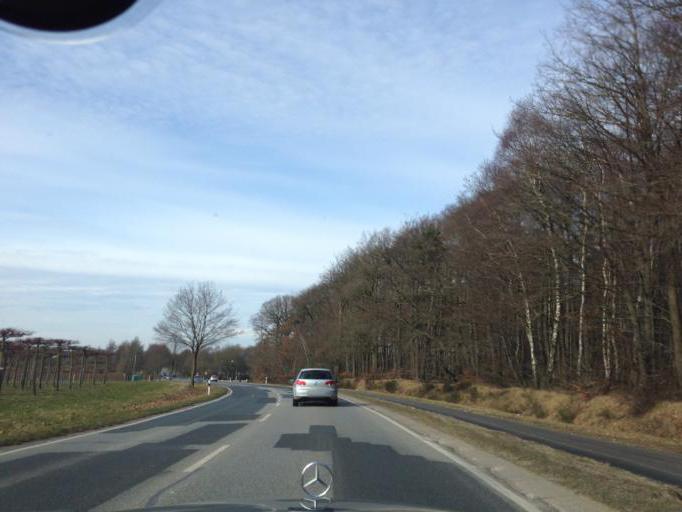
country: DE
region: Lower Saxony
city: Seevetal
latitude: 53.4360
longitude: 9.9173
